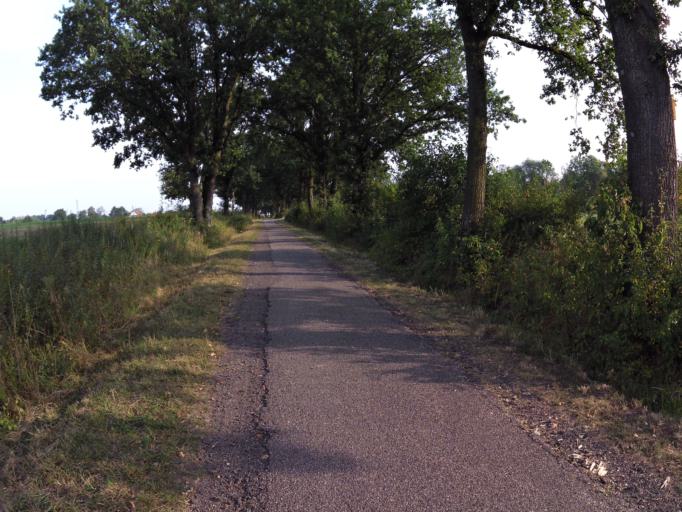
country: DE
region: North Rhine-Westphalia
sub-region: Regierungsbezirk Detmold
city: Petershagen
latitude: 52.3833
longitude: 8.9636
